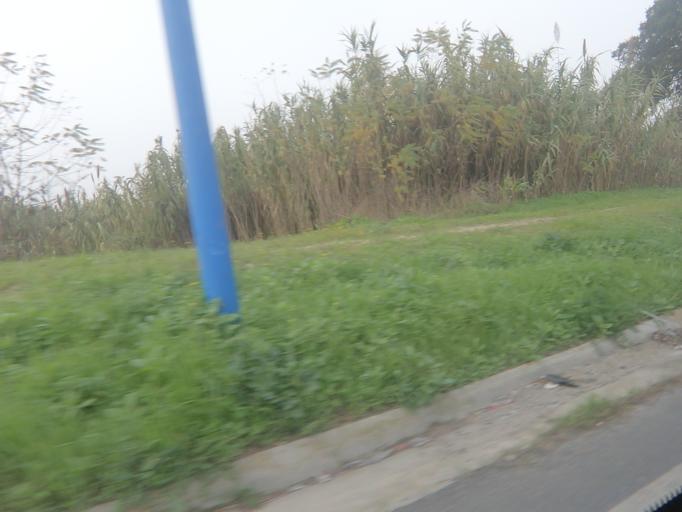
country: PT
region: Setubal
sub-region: Montijo
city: Montijo
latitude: 38.6888
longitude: -8.9463
